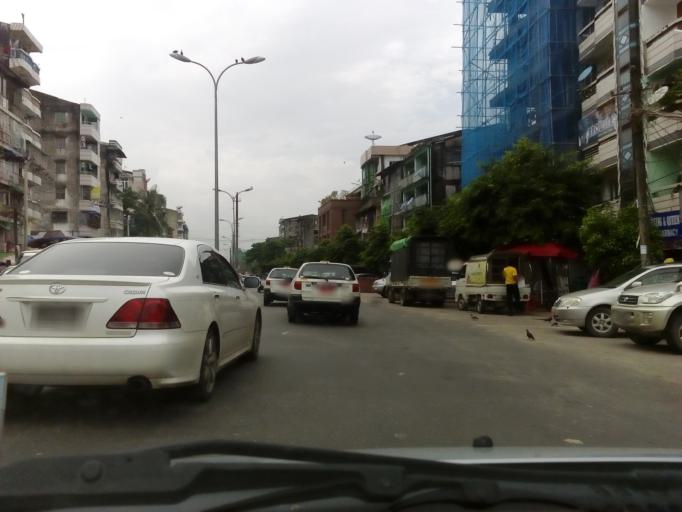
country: MM
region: Yangon
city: Yangon
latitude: 16.8123
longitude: 96.1708
